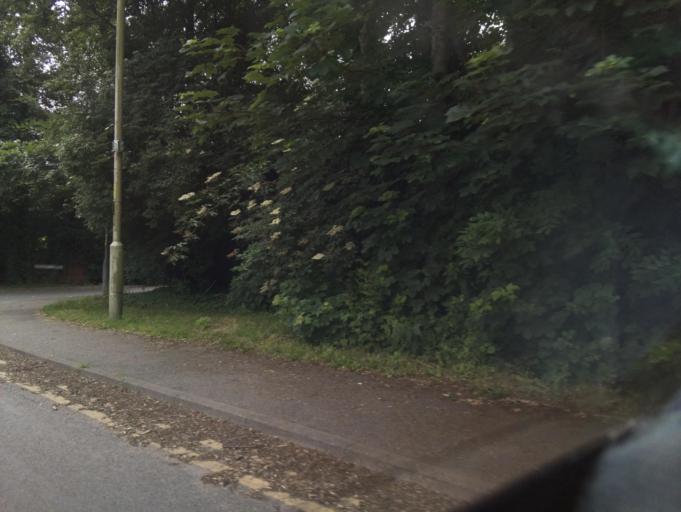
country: GB
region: England
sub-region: District of Rutland
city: Oakham
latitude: 52.6659
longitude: -0.7249
